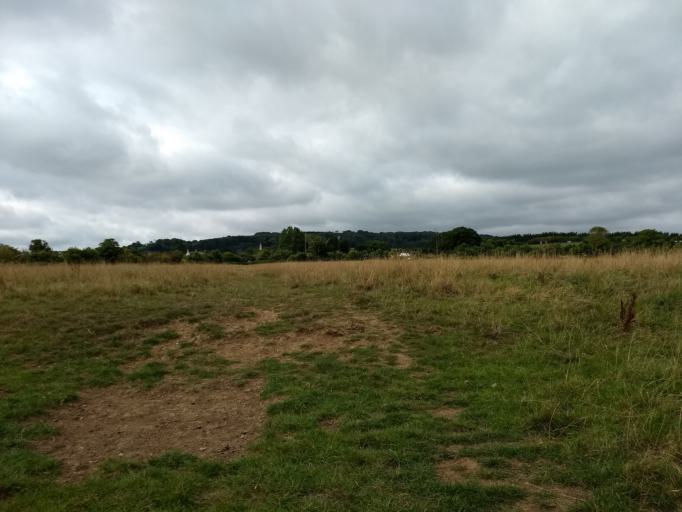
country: GB
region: England
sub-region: Isle of Wight
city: Brading
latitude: 50.6861
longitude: -1.1358
